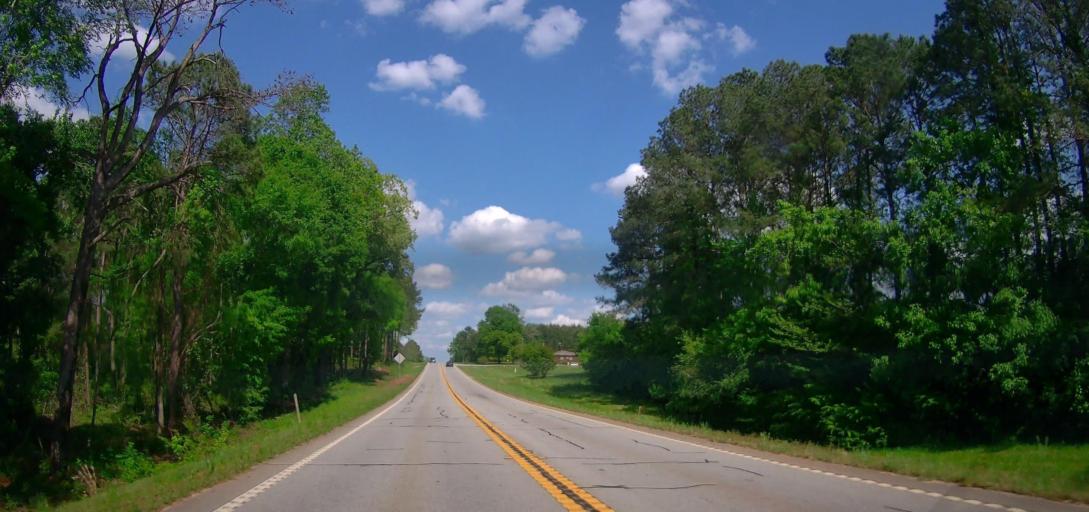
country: US
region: Georgia
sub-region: Greene County
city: Greensboro
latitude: 33.5709
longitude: -83.2360
